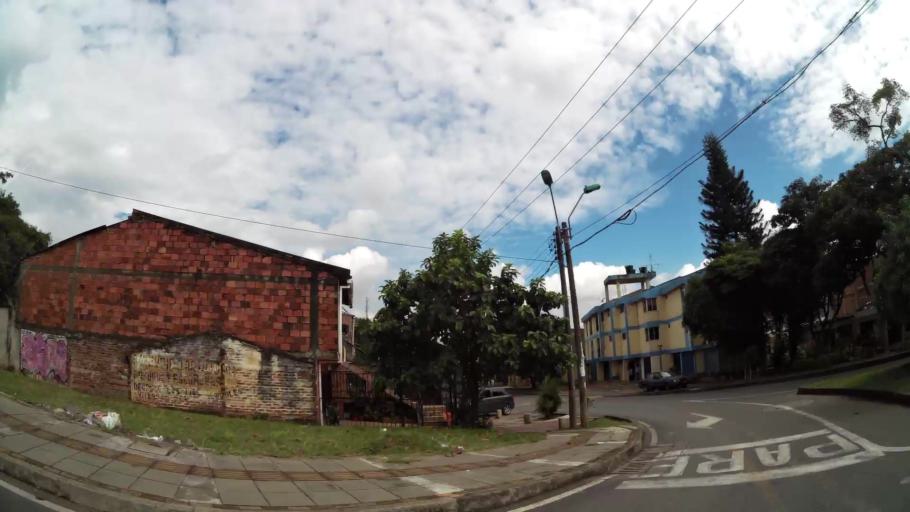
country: CO
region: Valle del Cauca
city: Cali
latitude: 3.3860
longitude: -76.5502
